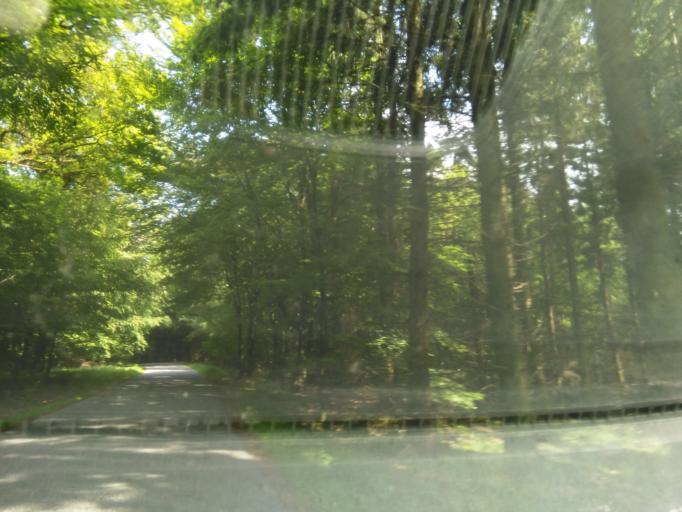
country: DK
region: Central Jutland
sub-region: Skanderborg Kommune
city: Galten
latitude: 56.2281
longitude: 9.9291
